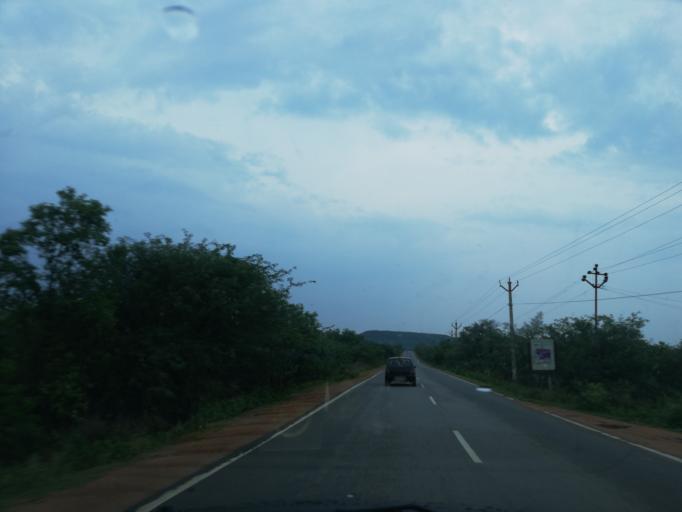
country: IN
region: Andhra Pradesh
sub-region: Guntur
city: Macherla
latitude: 16.6378
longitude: 79.2897
